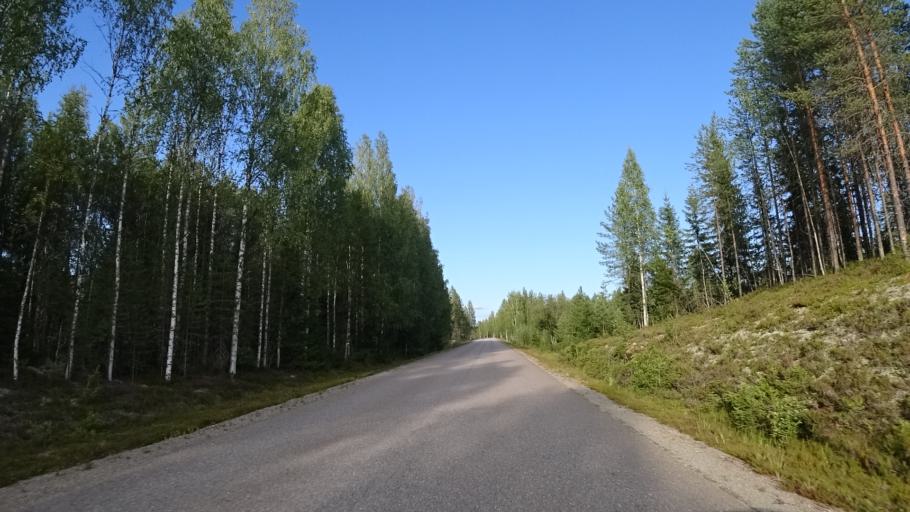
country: FI
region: North Karelia
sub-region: Joensuu
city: Eno
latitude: 63.0276
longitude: 30.5118
